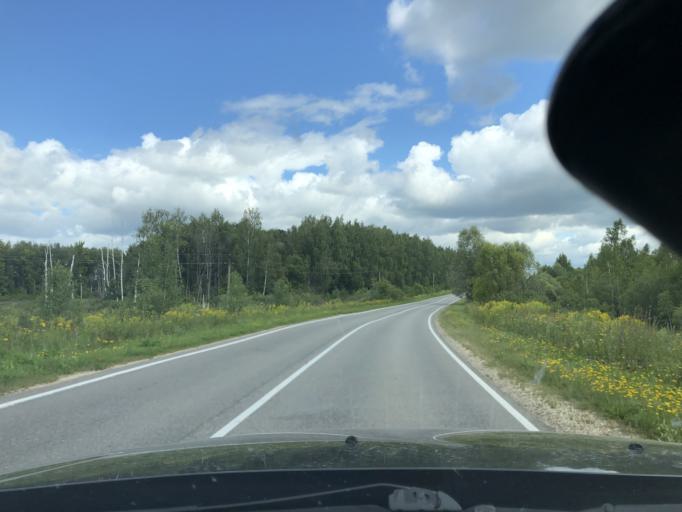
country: RU
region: Tula
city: Yasnogorsk
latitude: 54.4226
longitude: 37.6911
